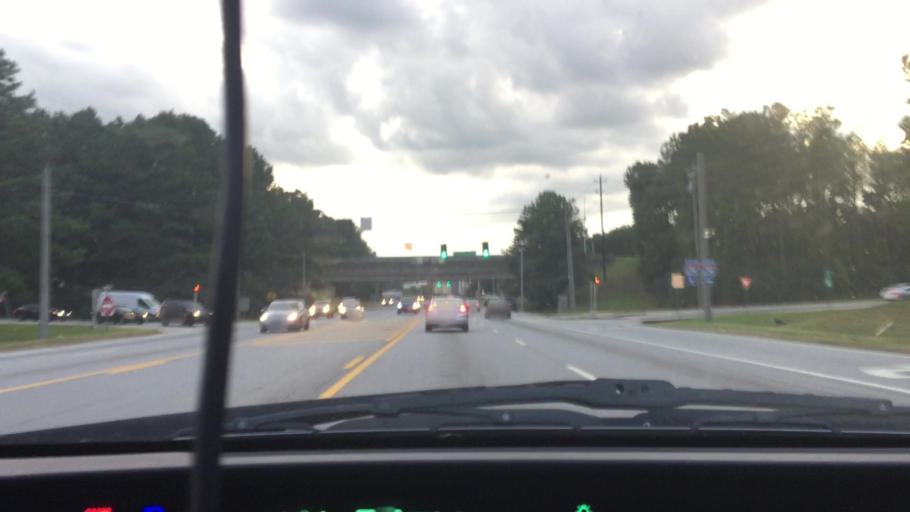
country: US
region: Georgia
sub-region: Henry County
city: Stockbridge
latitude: 33.5536
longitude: -84.2668
